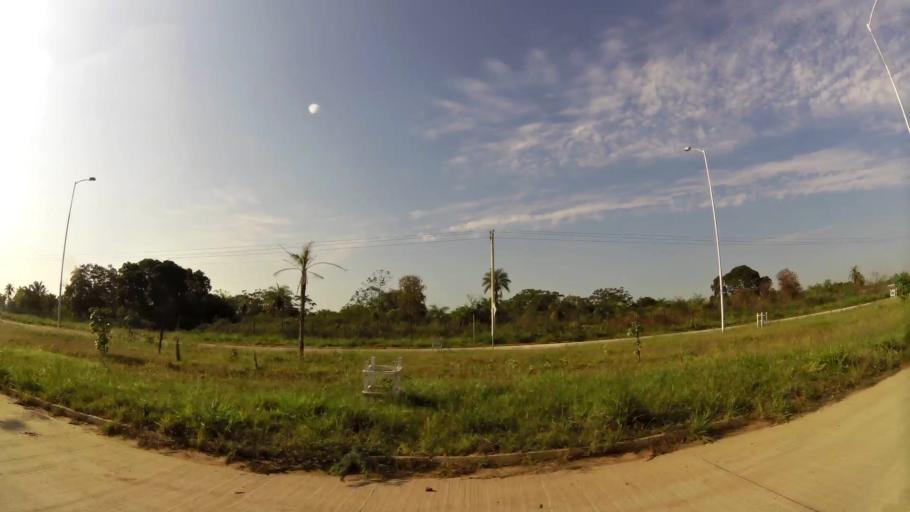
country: BO
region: Santa Cruz
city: Santa Cruz de la Sierra
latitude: -17.6921
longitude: -63.1169
